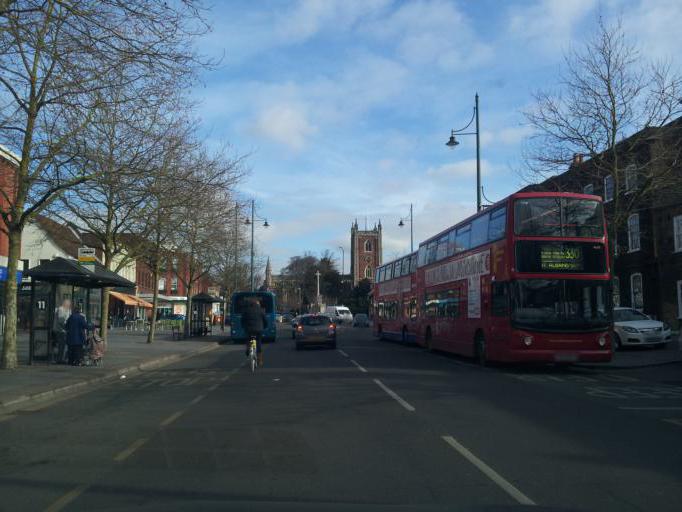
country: GB
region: England
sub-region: Hertfordshire
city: St Albans
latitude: 51.7541
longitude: -0.3369
